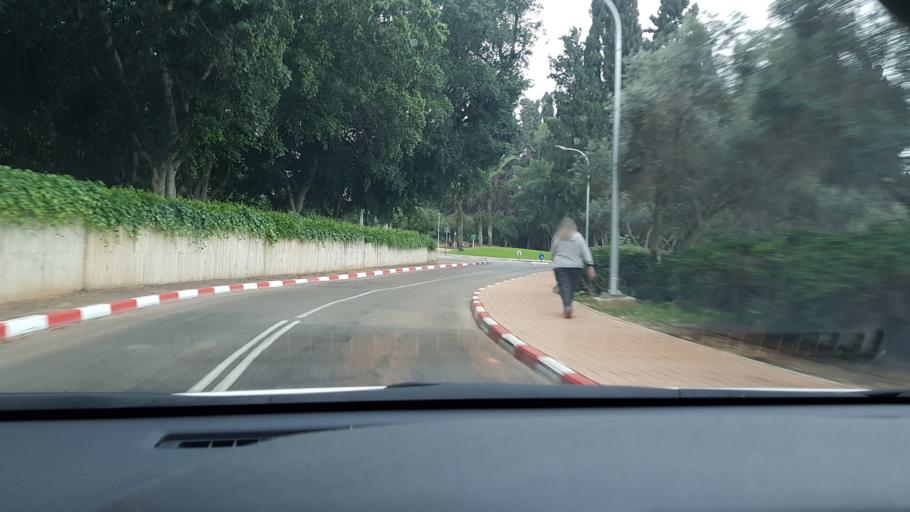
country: IL
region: Central District
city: Ness Ziona
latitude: 31.9087
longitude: 34.8187
